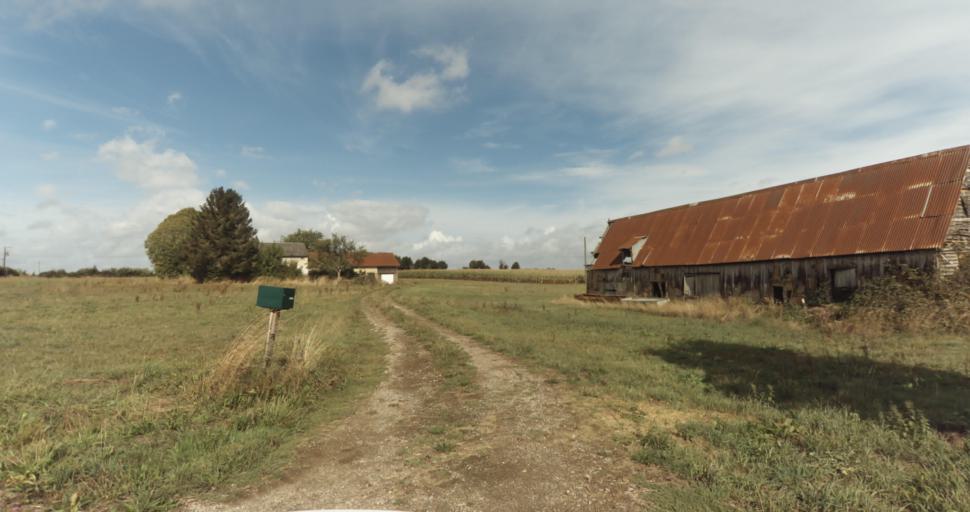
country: FR
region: Lower Normandy
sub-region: Departement de l'Orne
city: Gace
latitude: 48.8202
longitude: 0.3996
